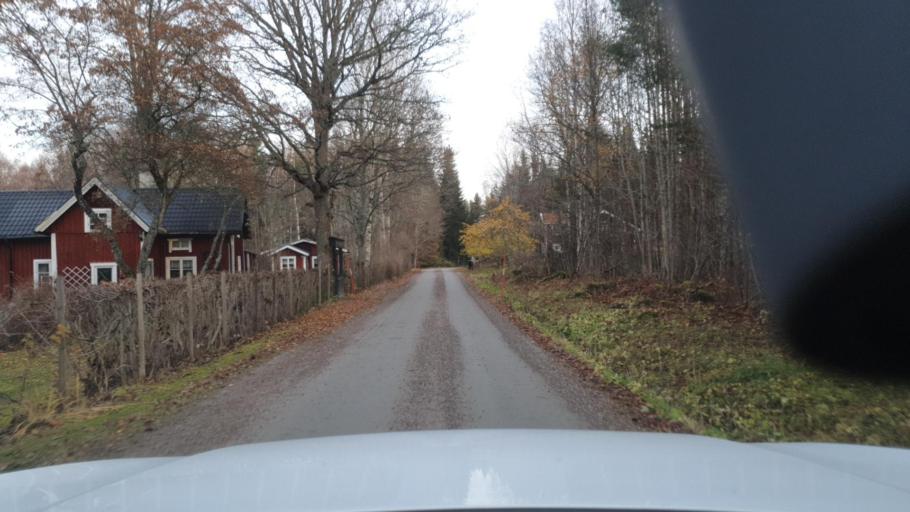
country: SE
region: Uppsala
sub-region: Alvkarleby Kommun
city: AElvkarleby
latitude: 60.4860
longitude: 17.4590
